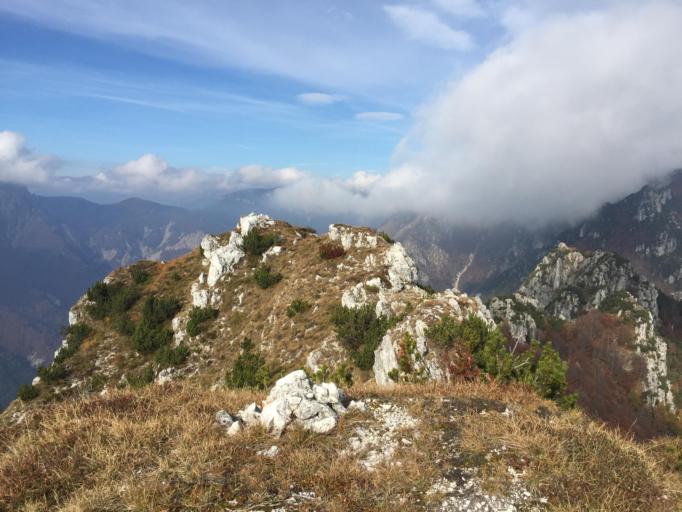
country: IT
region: Friuli Venezia Giulia
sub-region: Provincia di Udine
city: Moggio Udinese
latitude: 46.4521
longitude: 13.2102
